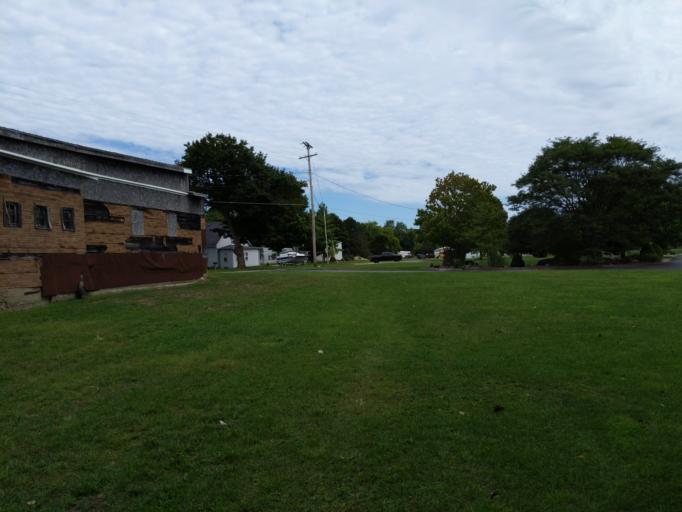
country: US
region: Michigan
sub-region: Barry County
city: Nashville
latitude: 42.6031
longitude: -85.0871
